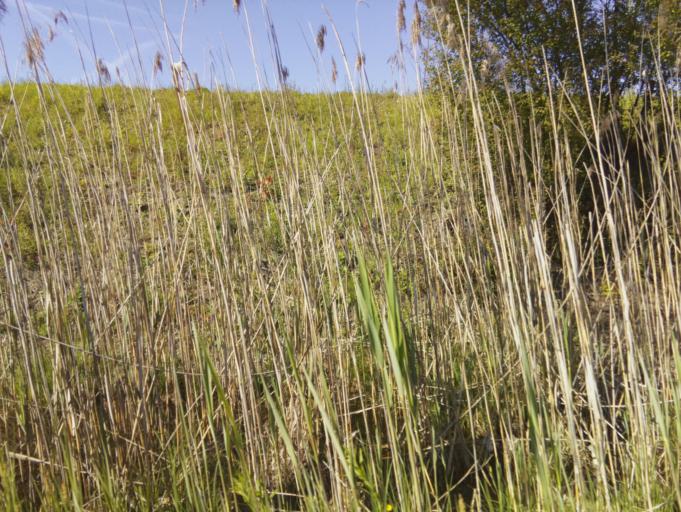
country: CH
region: Saint Gallen
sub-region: Wahlkreis See-Gaster
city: Jona
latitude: 47.2226
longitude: 8.8538
